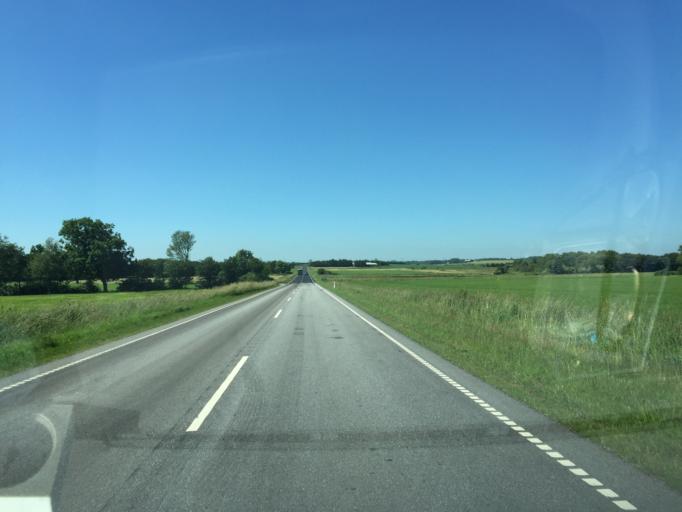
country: DK
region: South Denmark
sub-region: Haderslev Kommune
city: Vojens
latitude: 55.1554
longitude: 9.2546
